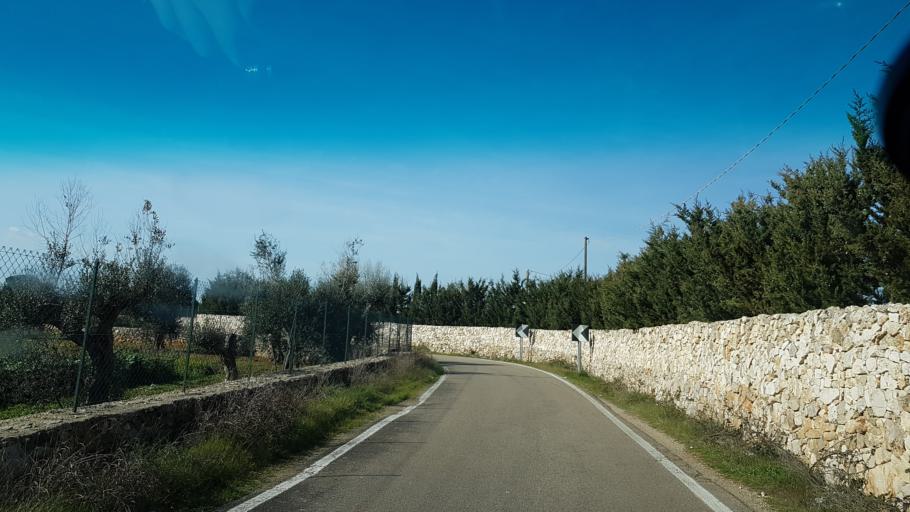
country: IT
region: Apulia
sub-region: Provincia di Lecce
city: Arnesano
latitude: 40.3504
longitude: 18.1172
